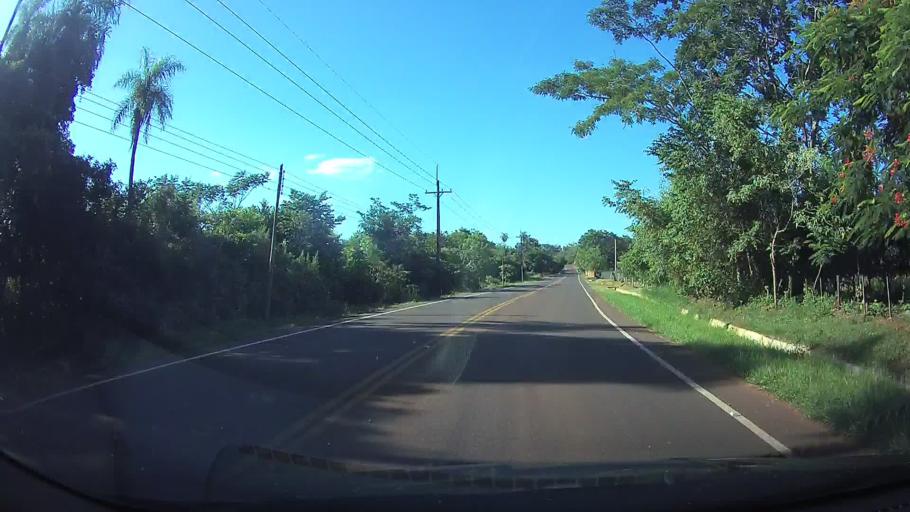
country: PY
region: Cordillera
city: Caacupe
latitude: -25.3393
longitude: -57.1552
